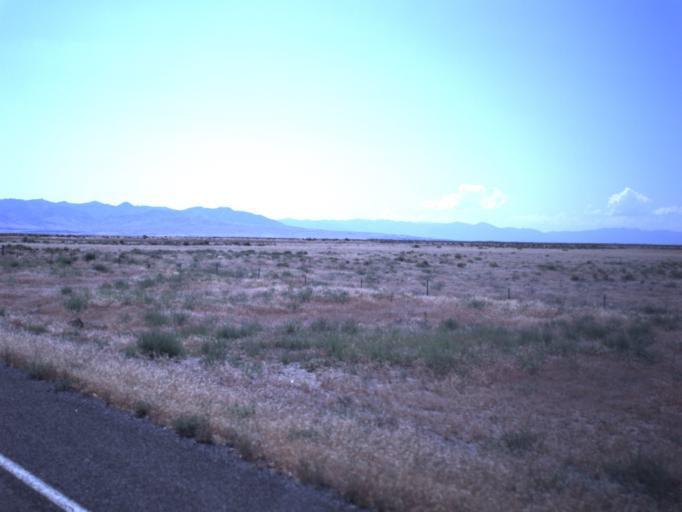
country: US
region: Utah
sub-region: Millard County
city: Delta
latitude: 39.4874
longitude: -112.5432
